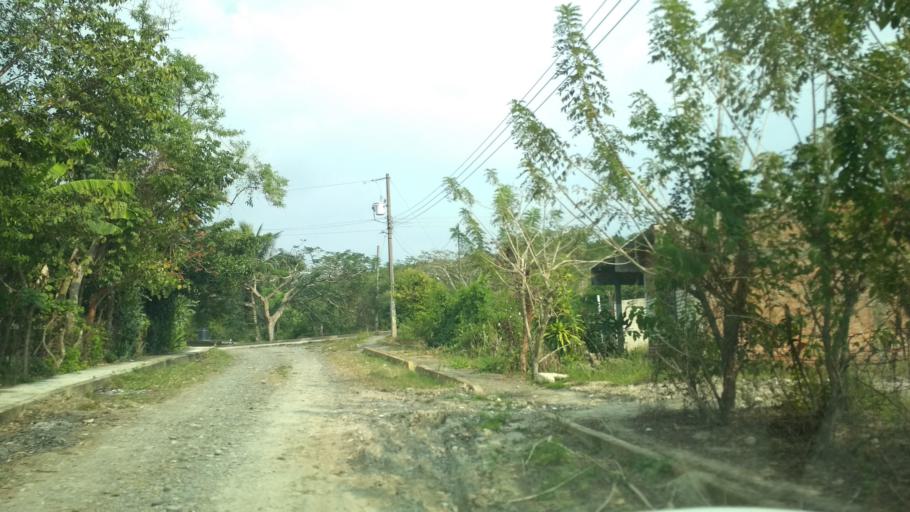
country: MM
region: Kayah
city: Loikaw
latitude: 20.2355
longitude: 97.2765
